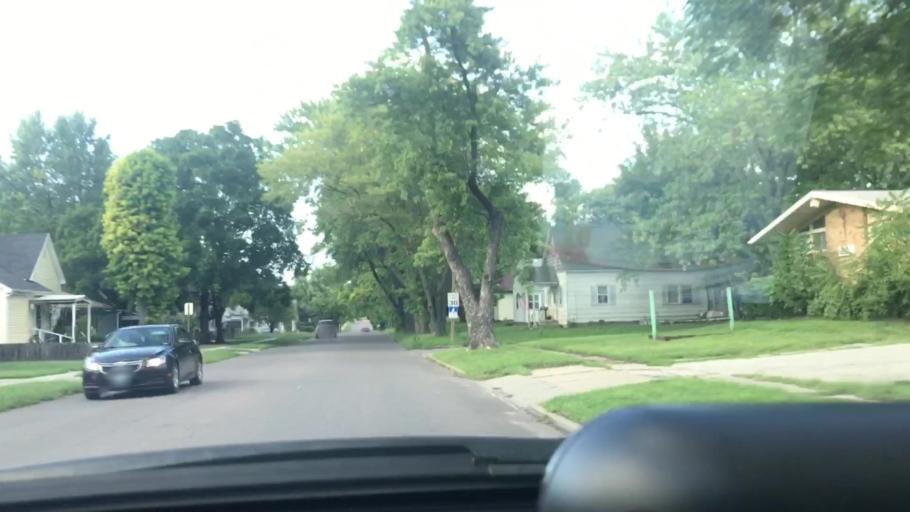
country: US
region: Missouri
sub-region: Pettis County
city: Sedalia
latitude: 38.6989
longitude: -93.2367
